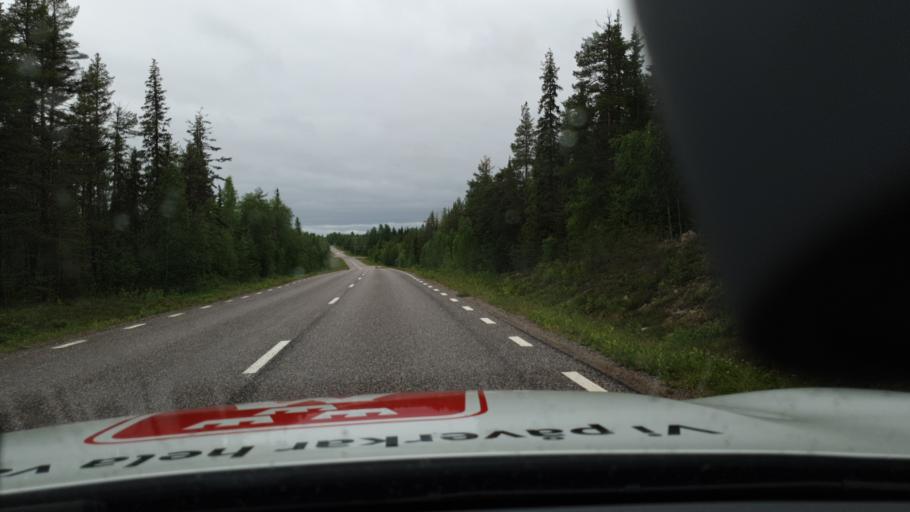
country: SE
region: Norrbotten
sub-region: Pajala Kommun
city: Pajala
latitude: 67.1849
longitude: 23.4869
